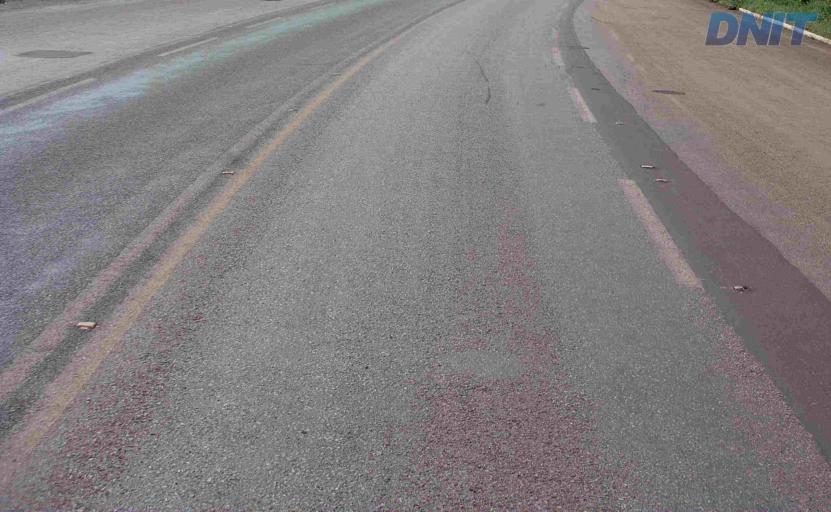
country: BR
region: Goias
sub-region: Barro Alto
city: Barro Alto
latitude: -14.9892
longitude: -48.9094
